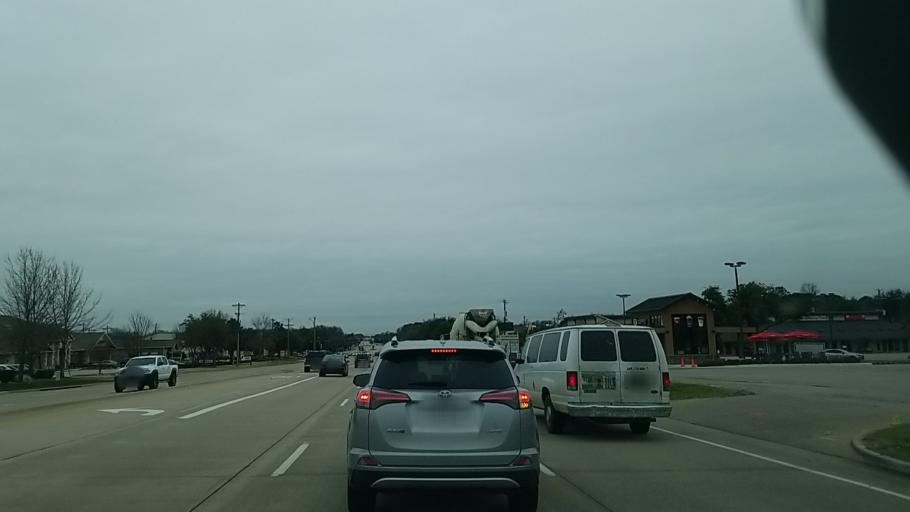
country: US
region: Texas
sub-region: Denton County
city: Flower Mound
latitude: 33.0325
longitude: -97.0708
